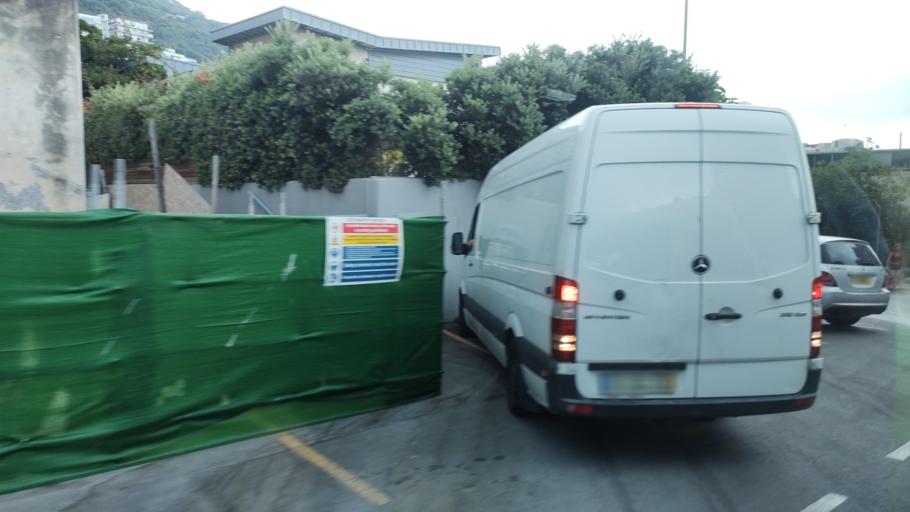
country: GI
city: Gibraltar
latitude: 36.1231
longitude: -5.3535
